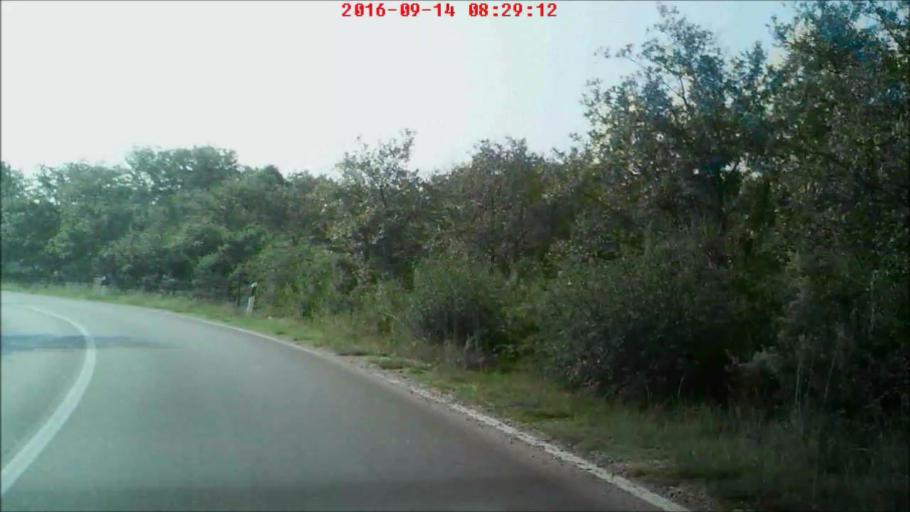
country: HR
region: Zadarska
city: Zadar
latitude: 44.1807
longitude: 15.2811
